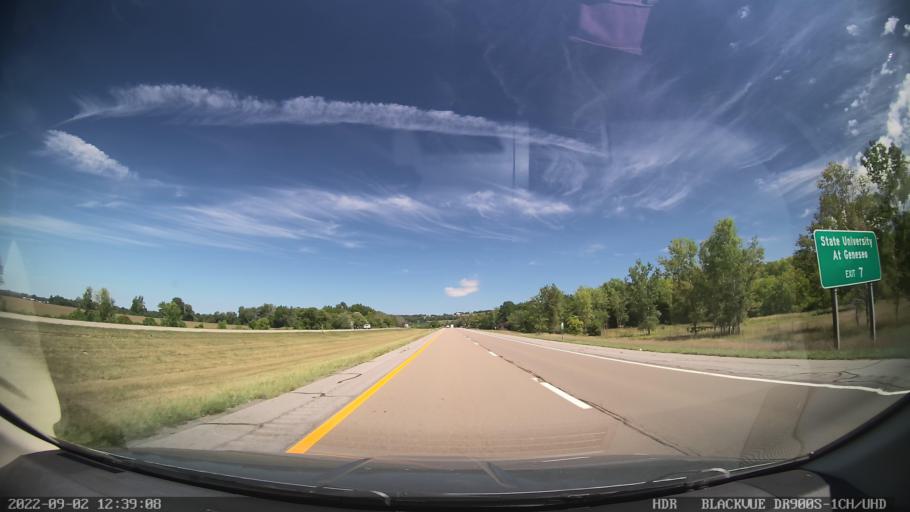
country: US
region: New York
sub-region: Livingston County
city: Mount Morris
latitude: 42.7171
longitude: -77.8338
